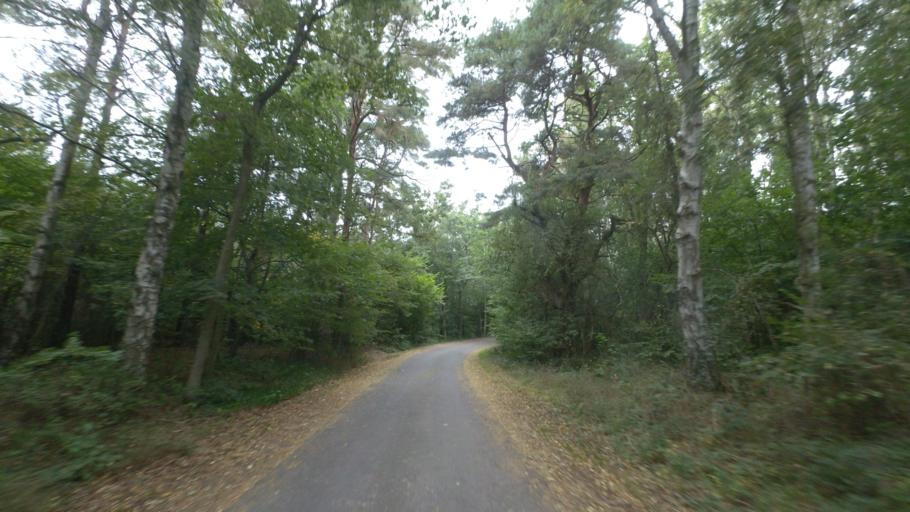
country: DK
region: Capital Region
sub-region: Bornholm Kommune
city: Nexo
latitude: 55.0014
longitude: 15.0379
